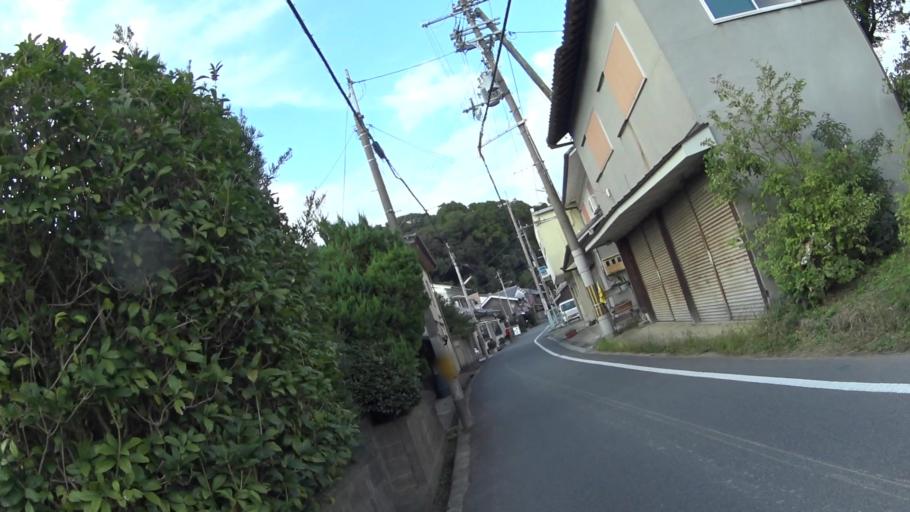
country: JP
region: Nara
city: Sakurai
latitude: 34.5375
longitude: 135.8416
